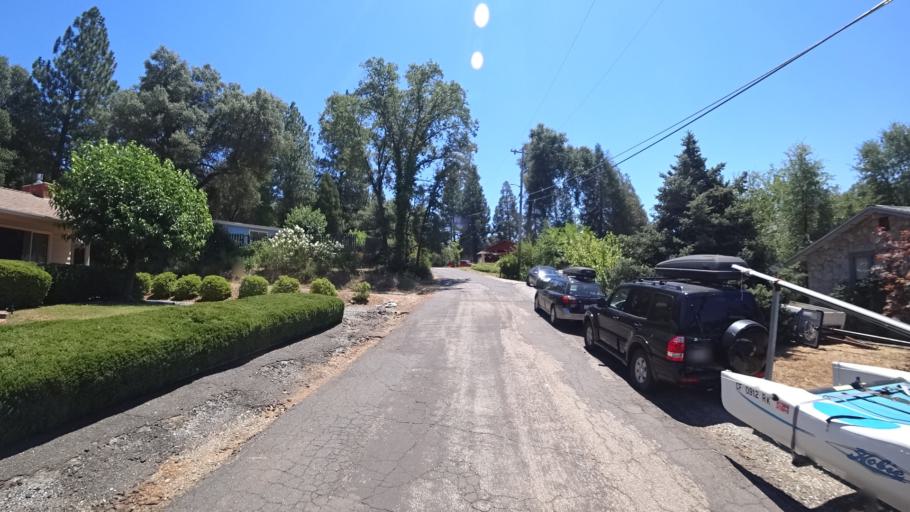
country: US
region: California
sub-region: Calaveras County
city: Murphys
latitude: 38.1360
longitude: -120.4542
